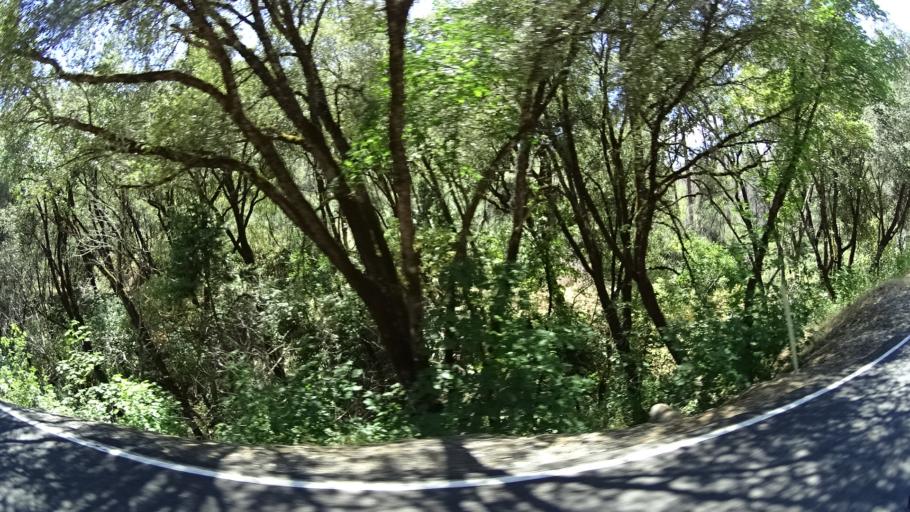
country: US
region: California
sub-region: Calaveras County
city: Mountain Ranch
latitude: 38.2182
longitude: -120.4677
